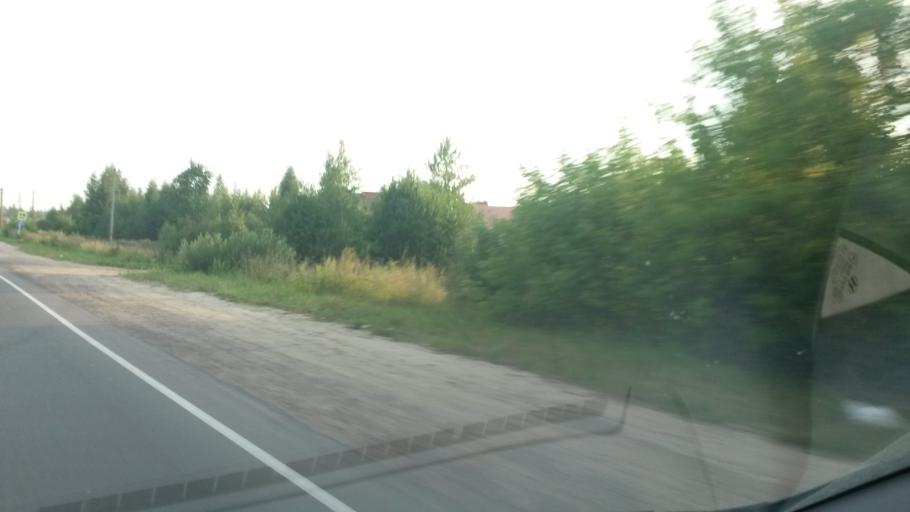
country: RU
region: Ivanovo
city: Novo-Talitsy
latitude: 57.0178
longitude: 40.8877
